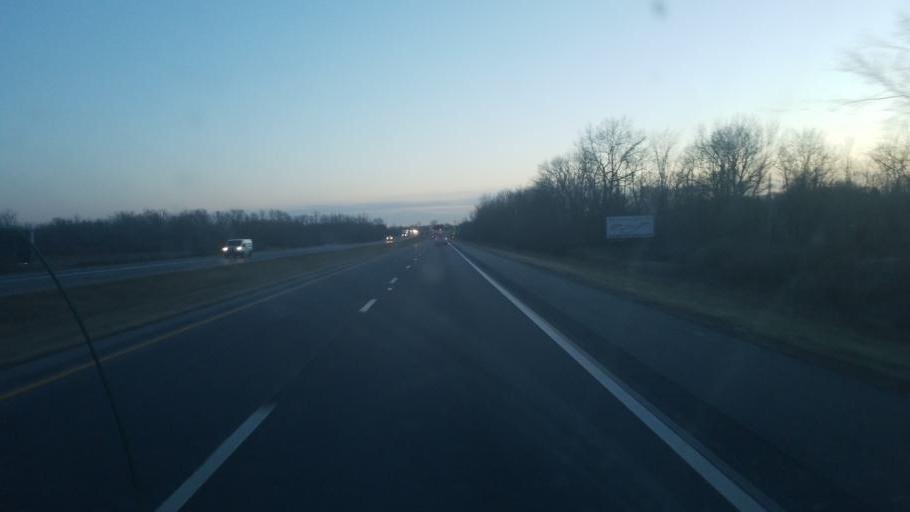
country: US
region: Ohio
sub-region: Marion County
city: Prospect
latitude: 40.4701
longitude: -83.0751
